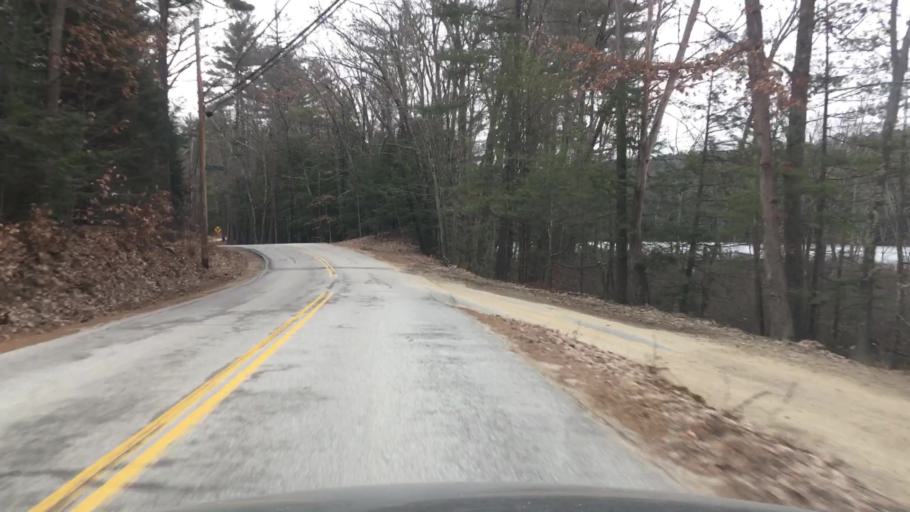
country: US
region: New Hampshire
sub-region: Hillsborough County
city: Mont Vernon
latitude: 42.9109
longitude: -71.5965
